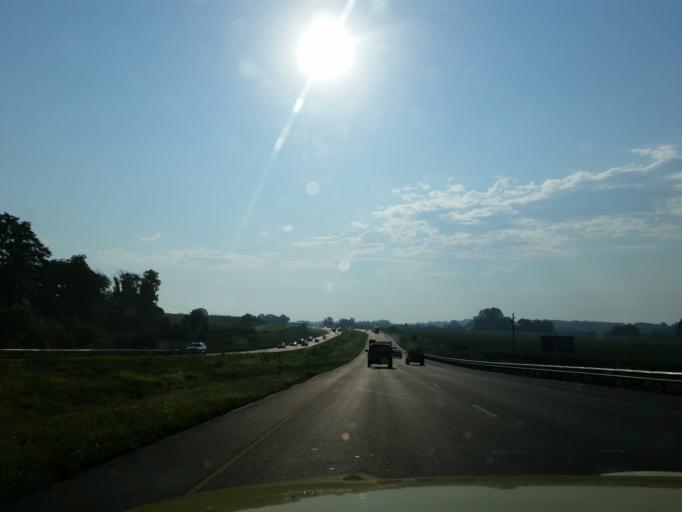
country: US
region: Pennsylvania
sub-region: Lancaster County
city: Columbia
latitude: 40.0379
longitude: -76.4678
